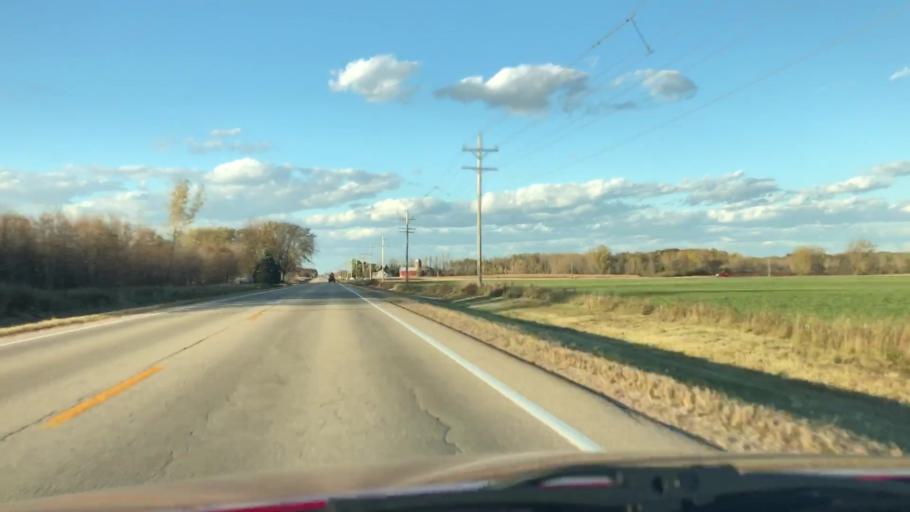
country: US
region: Wisconsin
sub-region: Outagamie County
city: Seymour
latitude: 44.4698
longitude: -88.2910
